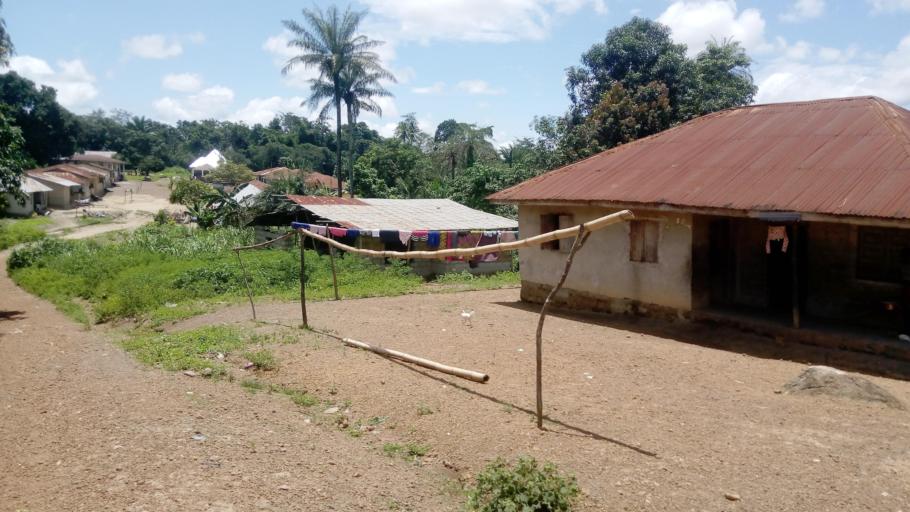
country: SL
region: Northern Province
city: Binkolo
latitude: 8.9195
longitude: -12.0073
